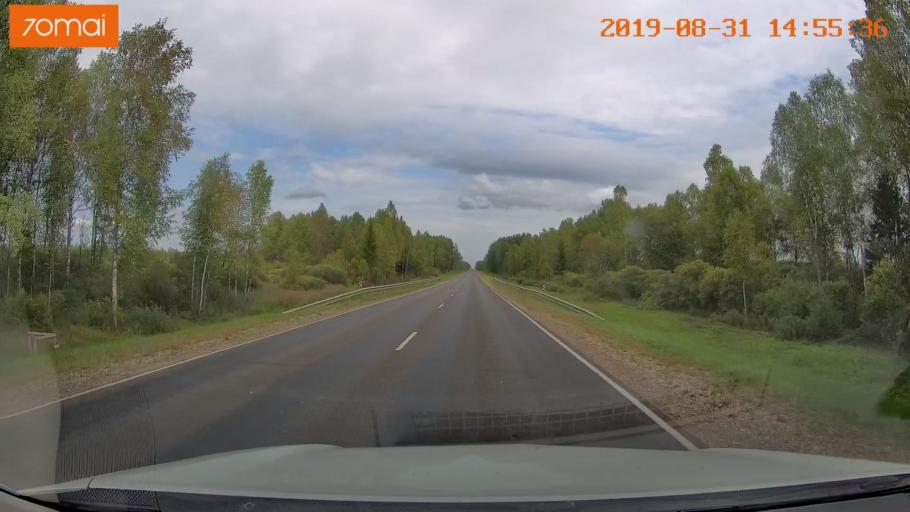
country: RU
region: Kaluga
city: Spas-Demensk
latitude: 54.2991
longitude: 33.9183
